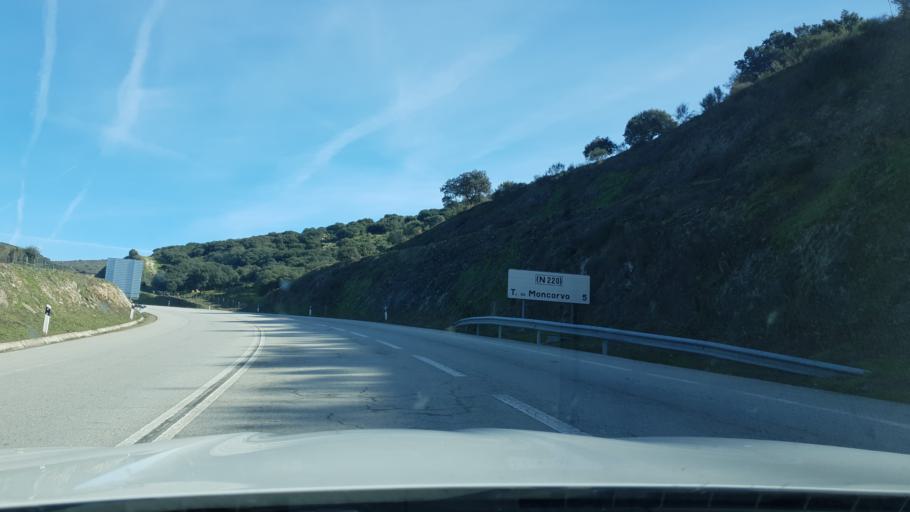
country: PT
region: Braganca
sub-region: Torre de Moncorvo
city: Torre de Moncorvo
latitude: 41.1814
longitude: -7.0983
